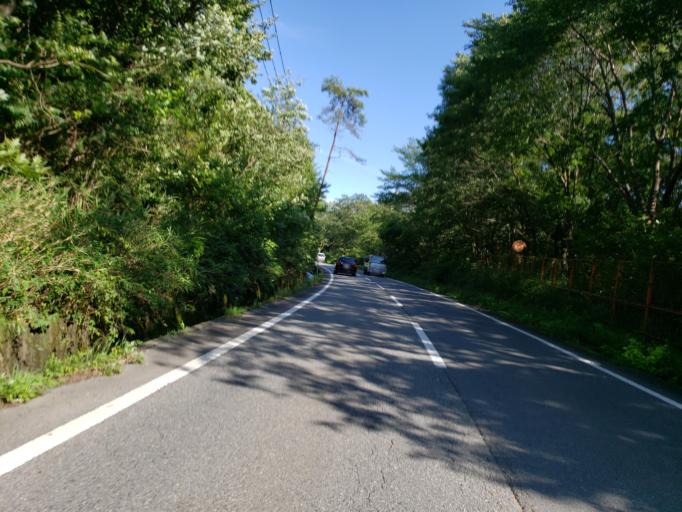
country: JP
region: Hyogo
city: Kakogawacho-honmachi
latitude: 34.8622
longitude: 134.7995
